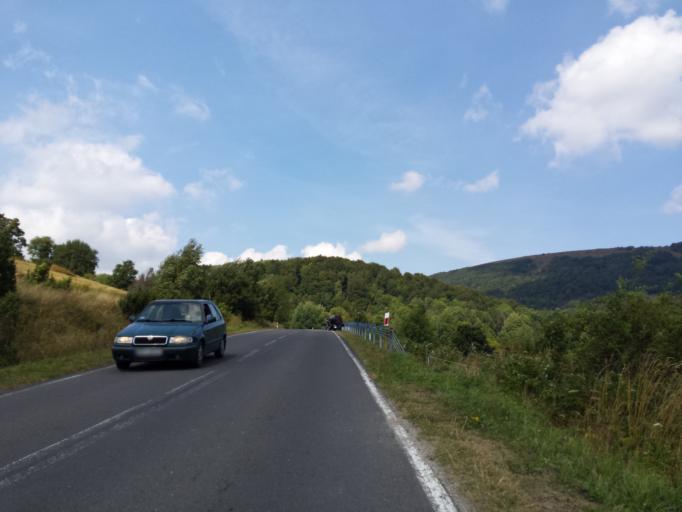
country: PL
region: Subcarpathian Voivodeship
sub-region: Powiat bieszczadzki
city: Lutowiska
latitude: 49.1392
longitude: 22.5536
